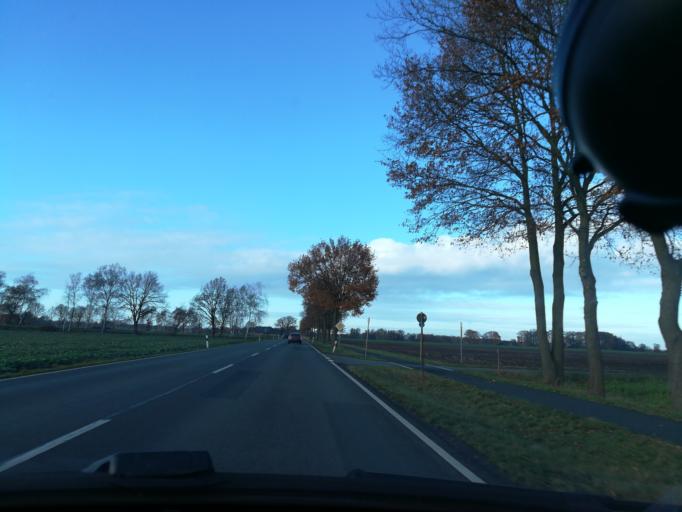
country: DE
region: Lower Saxony
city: Uchte
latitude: 52.4563
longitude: 8.9203
